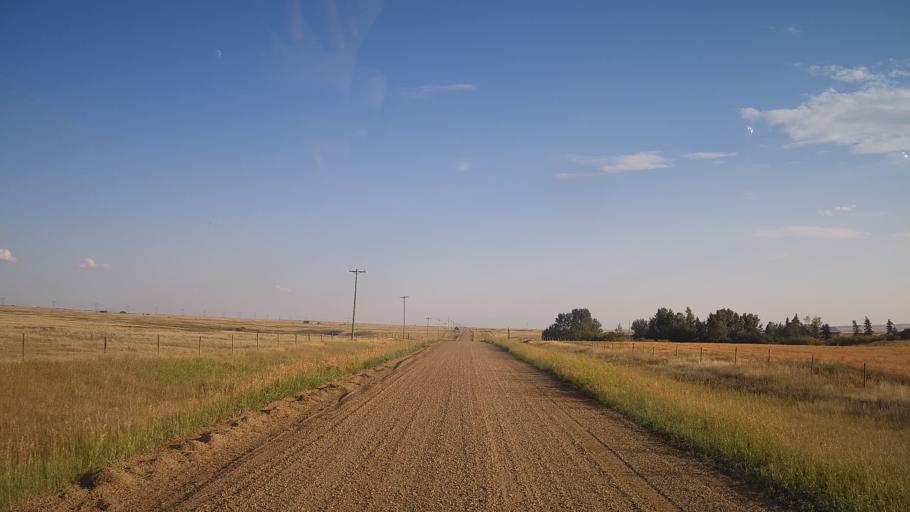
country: CA
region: Alberta
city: Hanna
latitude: 51.6149
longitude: -111.8569
